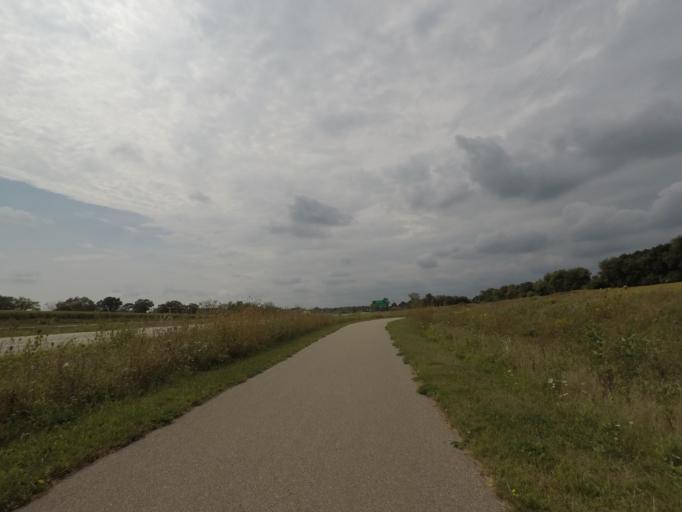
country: US
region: Wisconsin
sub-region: Jefferson County
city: Lake Koshkonong
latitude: 42.8489
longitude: -88.9161
